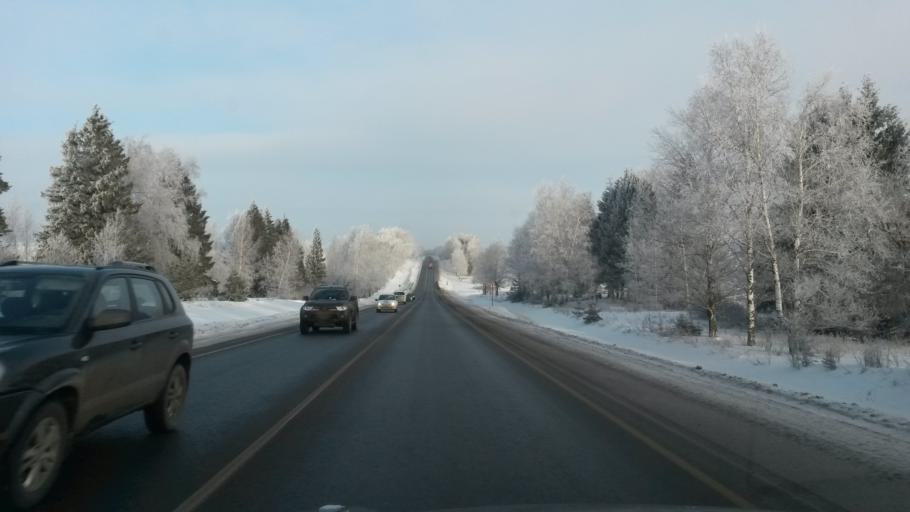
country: RU
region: Vladimir
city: Bogolyubovo
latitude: 56.2400
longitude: 40.4522
